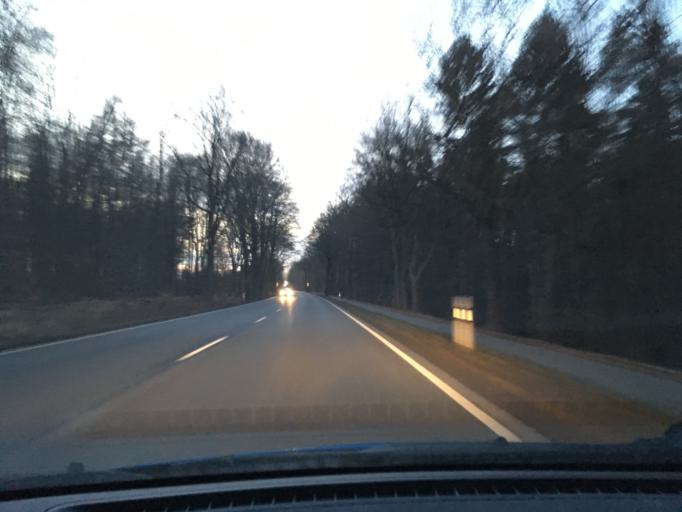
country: DE
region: Lower Saxony
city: Reinstorf
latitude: 53.2249
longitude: 10.5517
